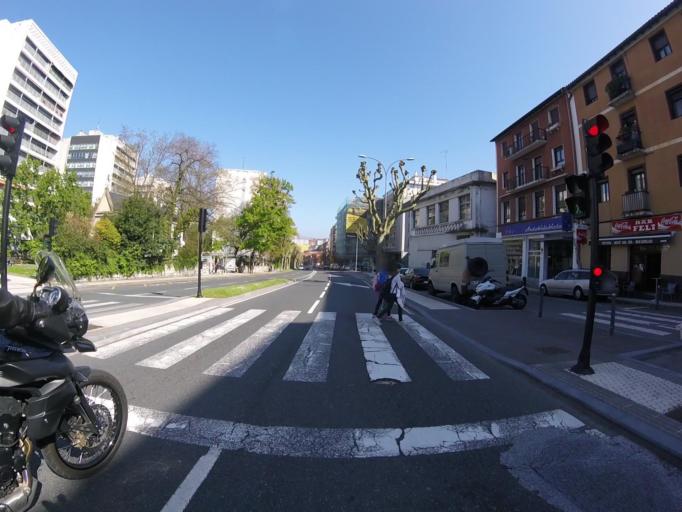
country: ES
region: Basque Country
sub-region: Provincia de Guipuzcoa
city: Pasaia
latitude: 43.3208
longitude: -1.9439
